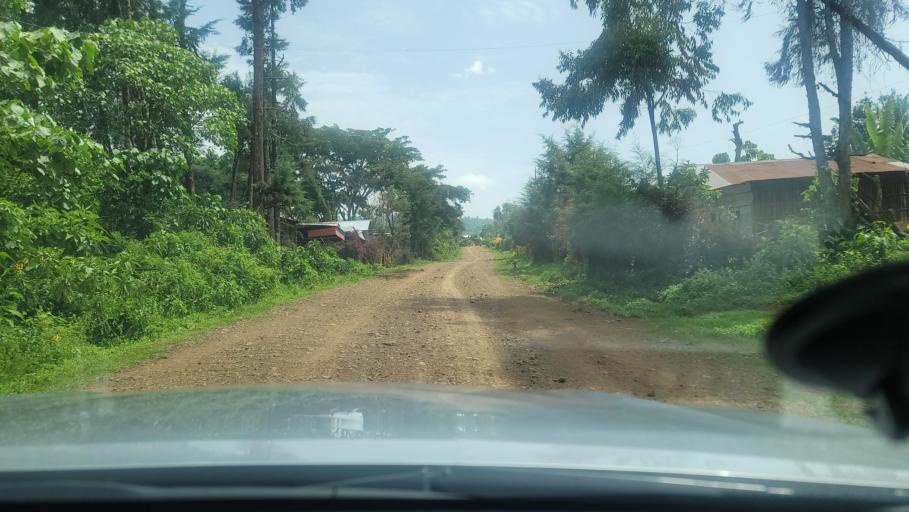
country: ET
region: Oromiya
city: Agaro
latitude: 7.7943
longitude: 36.4173
